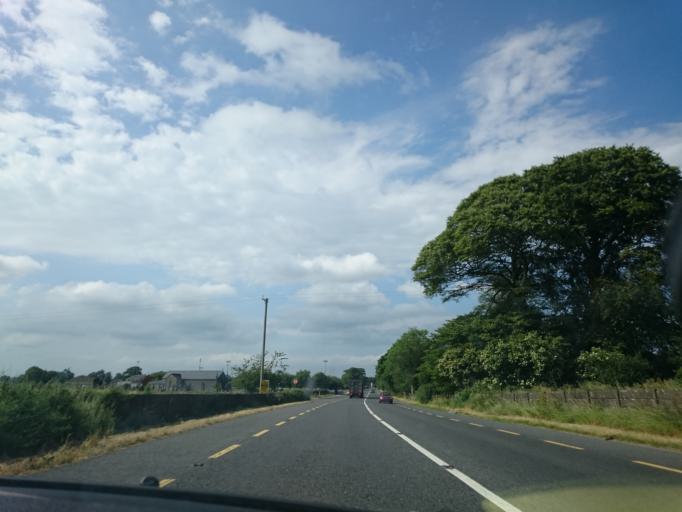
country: IE
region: Leinster
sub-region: Kilkenny
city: Kilkenny
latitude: 52.6206
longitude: -7.2492
